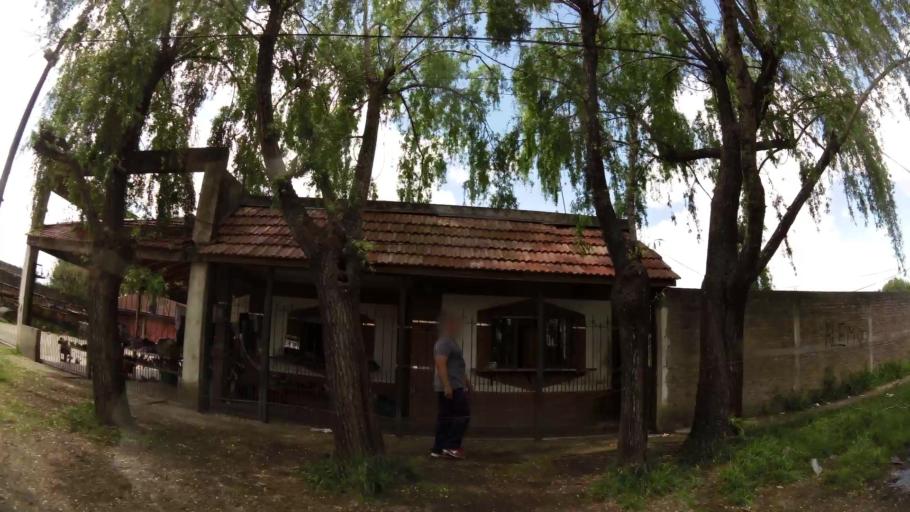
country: AR
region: Buenos Aires
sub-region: Partido de Quilmes
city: Quilmes
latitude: -34.8393
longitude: -58.2349
